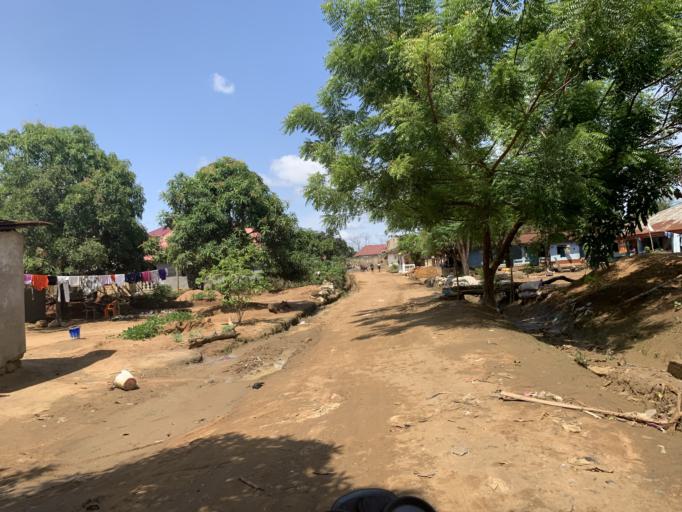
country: SL
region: Western Area
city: Waterloo
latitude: 8.3370
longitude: -13.0500
